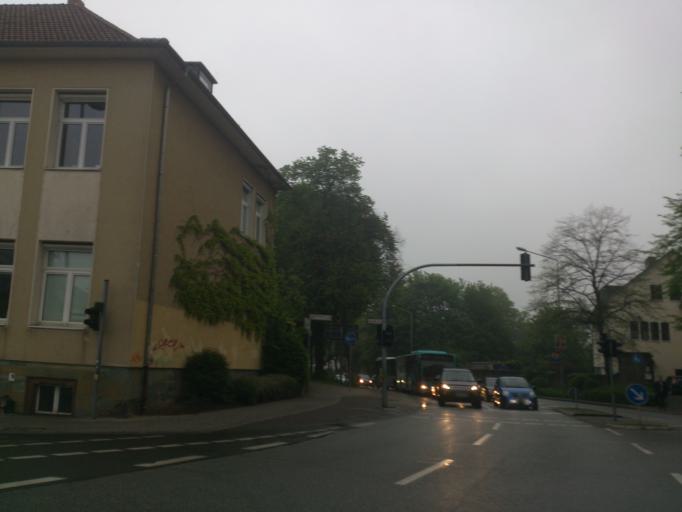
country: DE
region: North Rhine-Westphalia
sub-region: Regierungsbezirk Detmold
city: Paderborn
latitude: 51.7161
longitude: 8.7599
